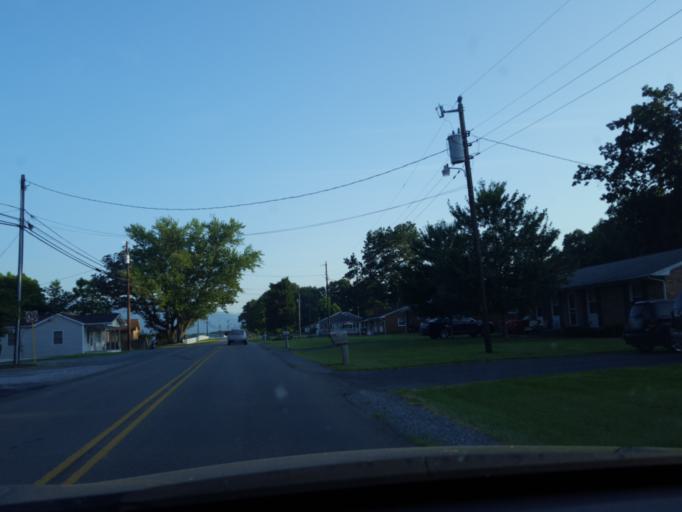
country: US
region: Virginia
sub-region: Augusta County
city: Lyndhurst
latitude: 38.0224
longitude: -78.9462
